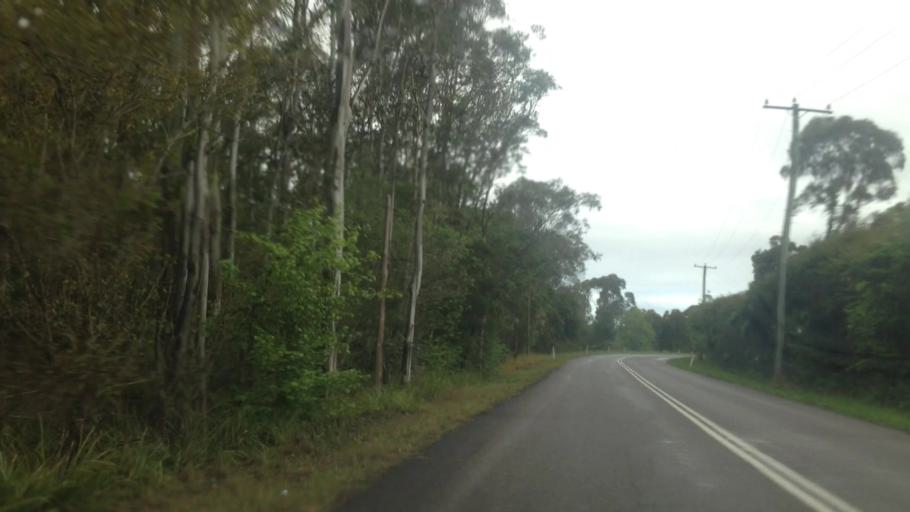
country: AU
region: New South Wales
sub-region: Wyong Shire
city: Little Jilliby
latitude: -33.2533
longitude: 151.3834
